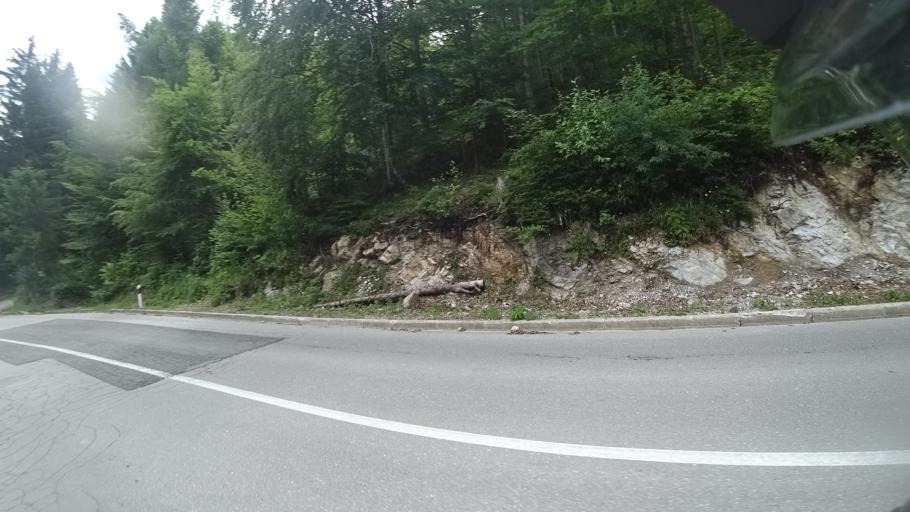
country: SI
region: Osilnica
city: Osilnica
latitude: 45.5959
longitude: 14.6310
